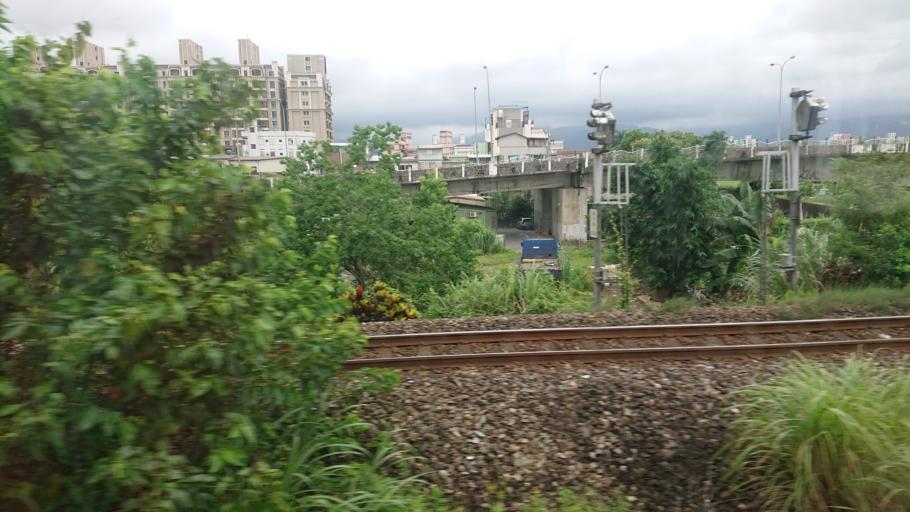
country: TW
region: Taiwan
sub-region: Yilan
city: Yilan
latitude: 24.7620
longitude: 121.7612
